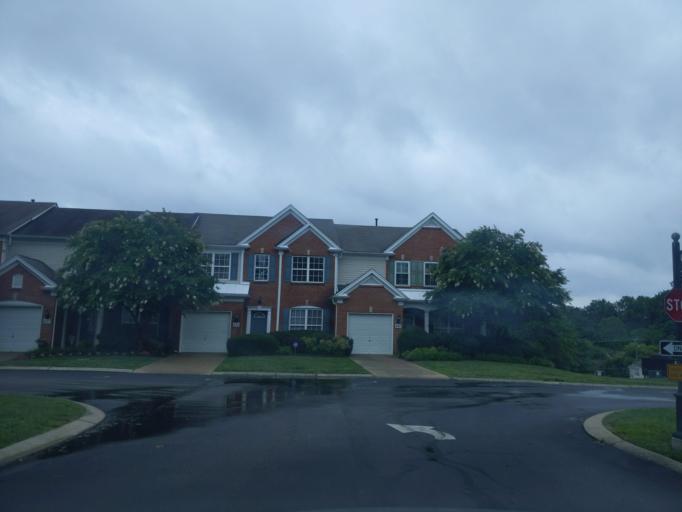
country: US
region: Tennessee
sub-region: Williamson County
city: Brentwood
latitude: 36.0410
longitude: -86.7562
